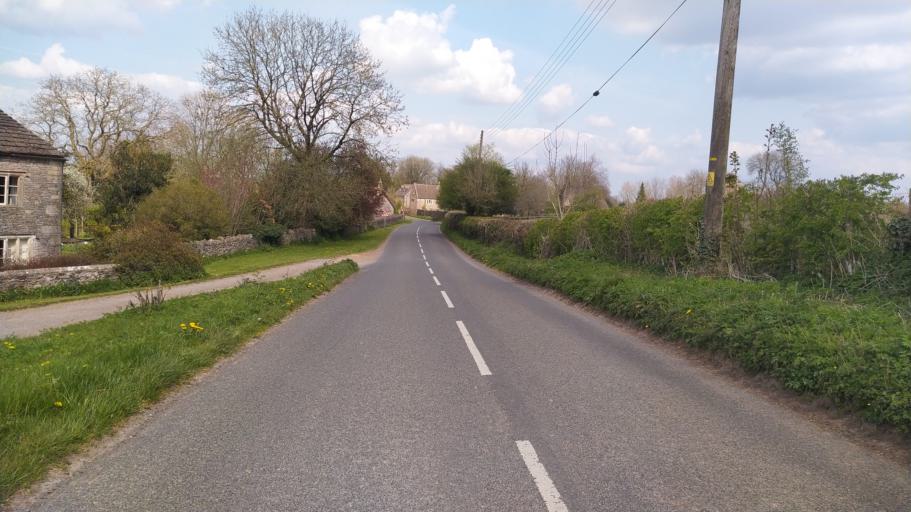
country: GB
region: England
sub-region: Bath and North East Somerset
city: Radstock
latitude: 51.2332
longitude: -2.4033
